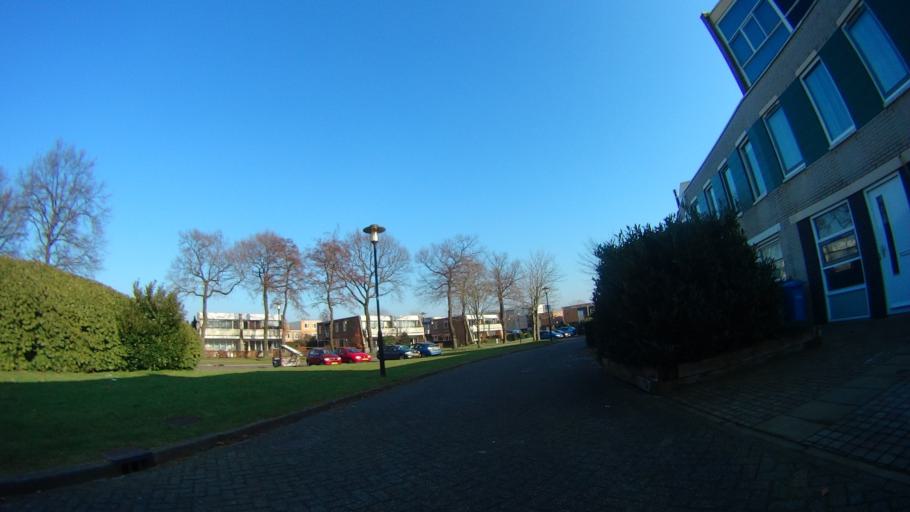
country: NL
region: Utrecht
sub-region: Gemeente Amersfoort
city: Hoogland
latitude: 52.1842
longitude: 5.3861
